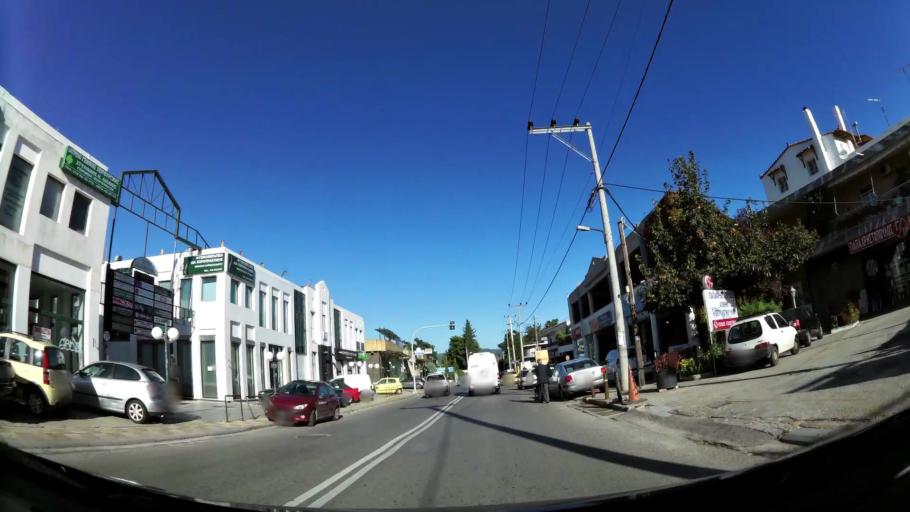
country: GR
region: Attica
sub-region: Nomarchia Anatolikis Attikis
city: Anoixi
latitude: 38.1349
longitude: 23.8578
